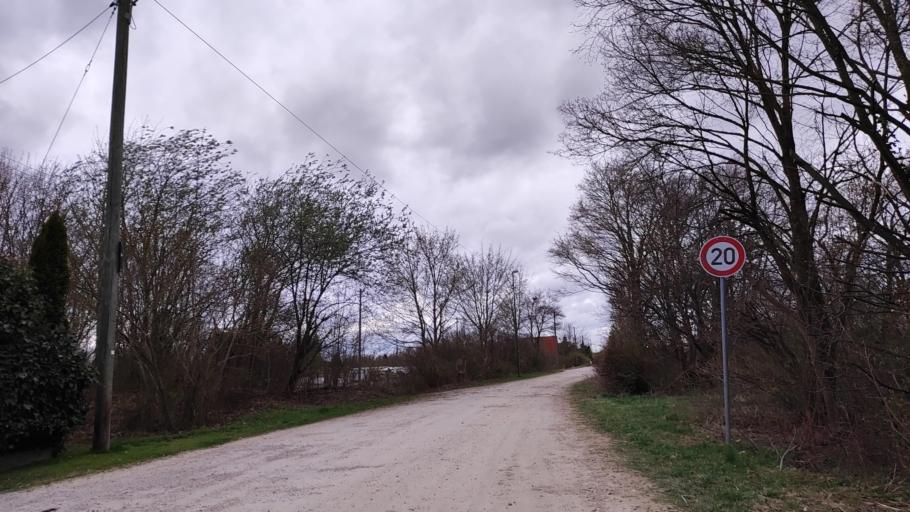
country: DE
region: Bavaria
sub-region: Swabia
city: Gersthofen
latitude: 48.3933
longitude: 10.8717
